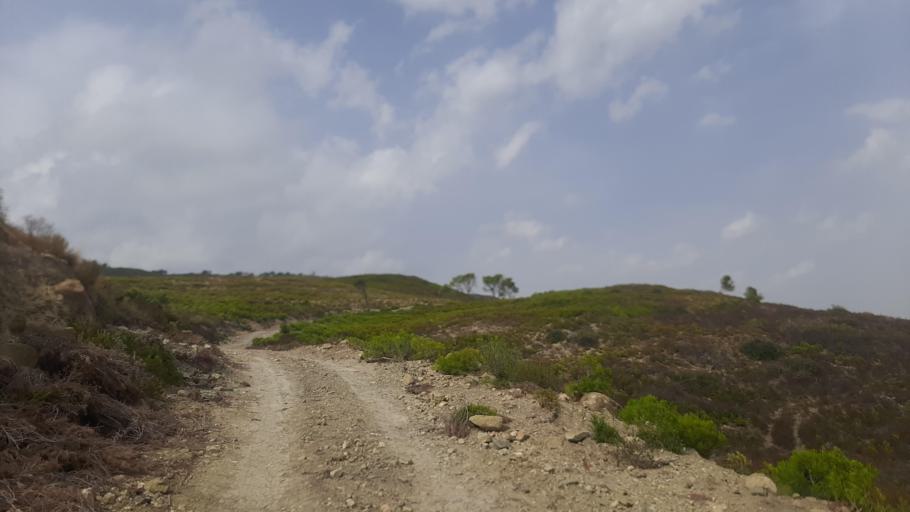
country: TN
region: Zaghwan
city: El Fahs
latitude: 36.1966
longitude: 9.8549
